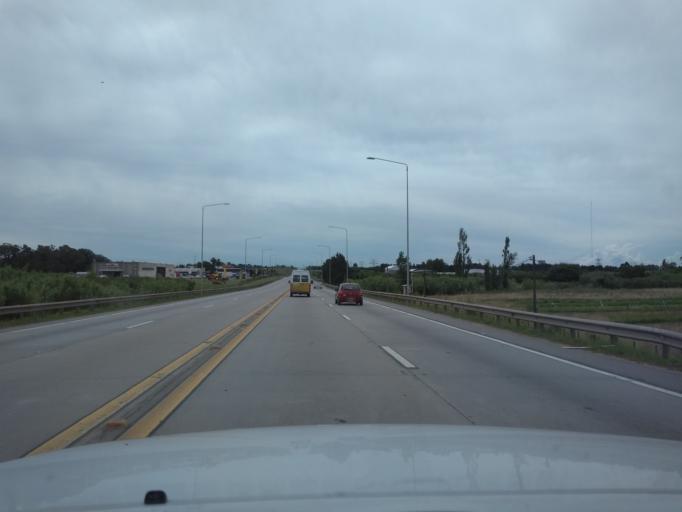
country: UY
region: Canelones
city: La Paz
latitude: -34.7947
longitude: -56.2041
